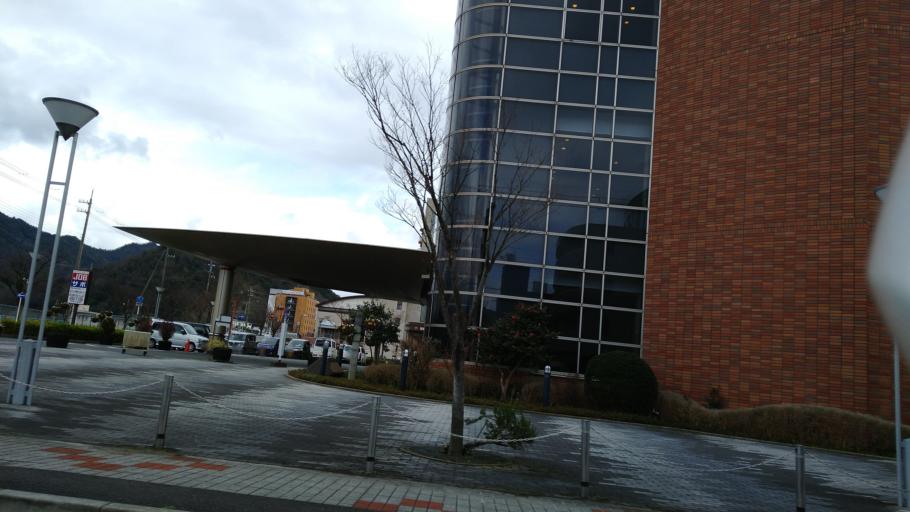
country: JP
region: Kyoto
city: Maizuru
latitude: 35.4770
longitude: 135.3947
